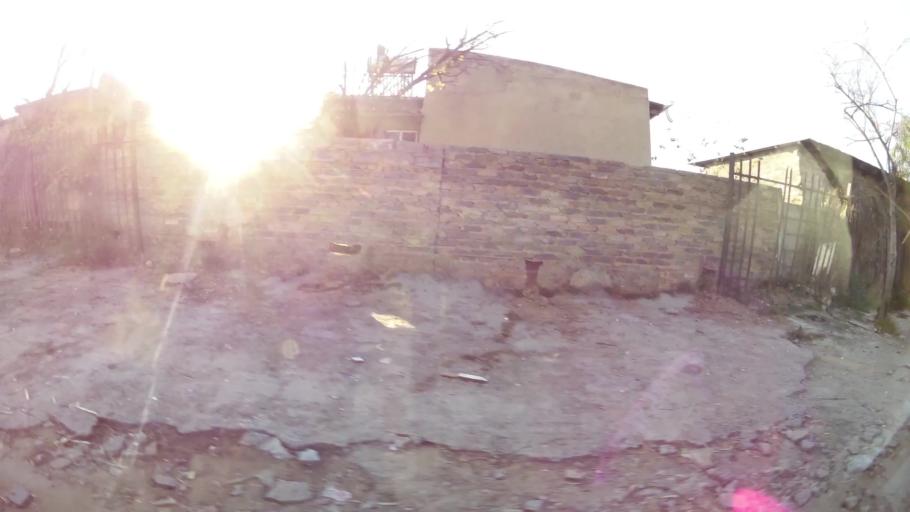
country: ZA
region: Gauteng
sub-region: City of Johannesburg Metropolitan Municipality
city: Modderfontein
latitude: -26.0892
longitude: 28.1126
